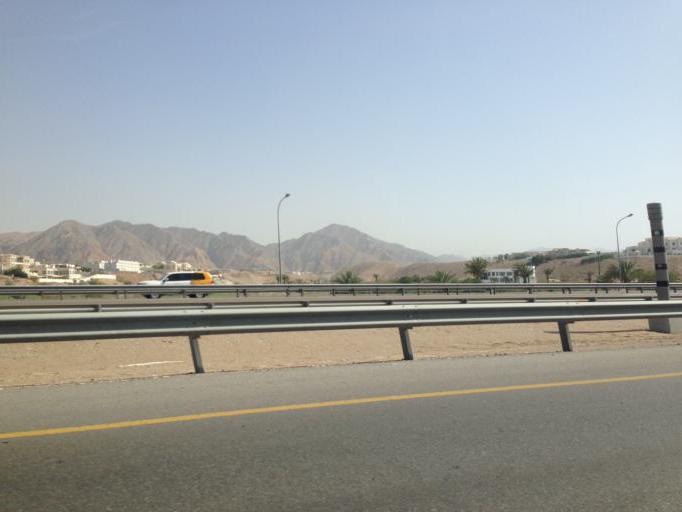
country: OM
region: Muhafazat Masqat
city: Bawshar
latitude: 23.5641
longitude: 58.3921
